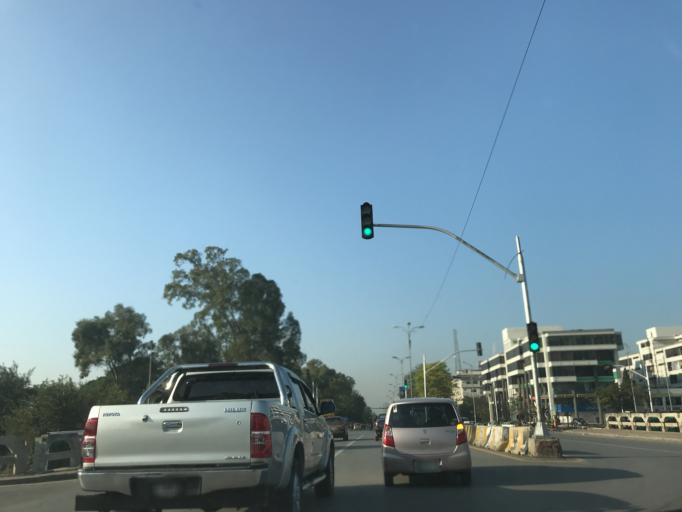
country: PK
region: Islamabad
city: Islamabad
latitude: 33.7171
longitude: 73.0726
